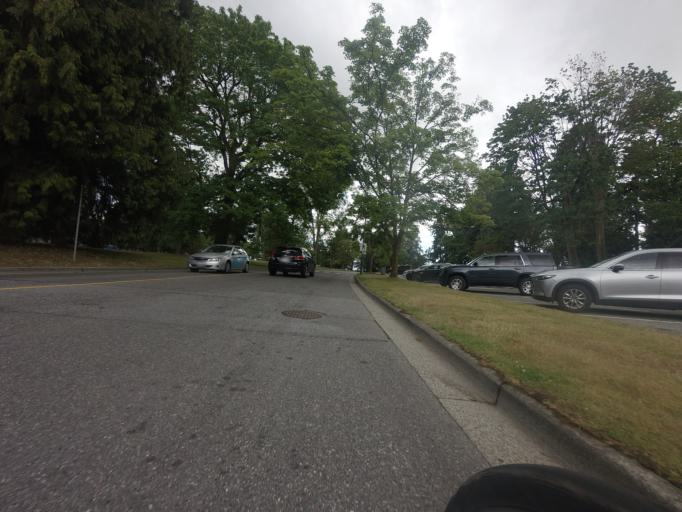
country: CA
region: British Columbia
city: West End
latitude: 49.2932
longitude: -123.1481
